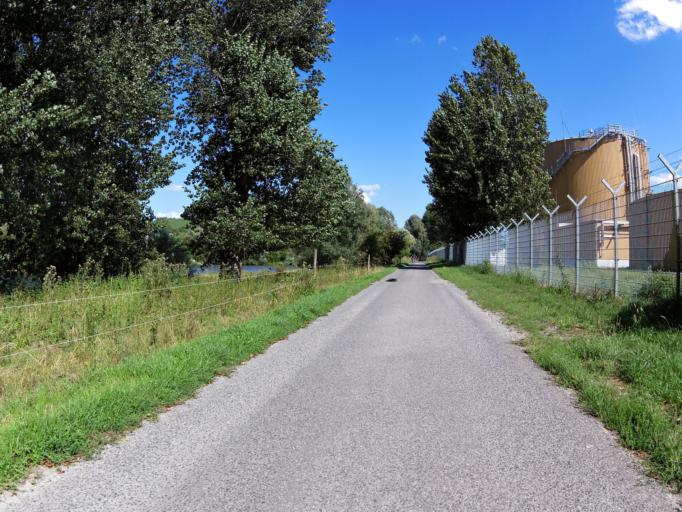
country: DE
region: Bavaria
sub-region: Regierungsbezirk Unterfranken
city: Frickenhausen
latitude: 49.6689
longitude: 10.0853
